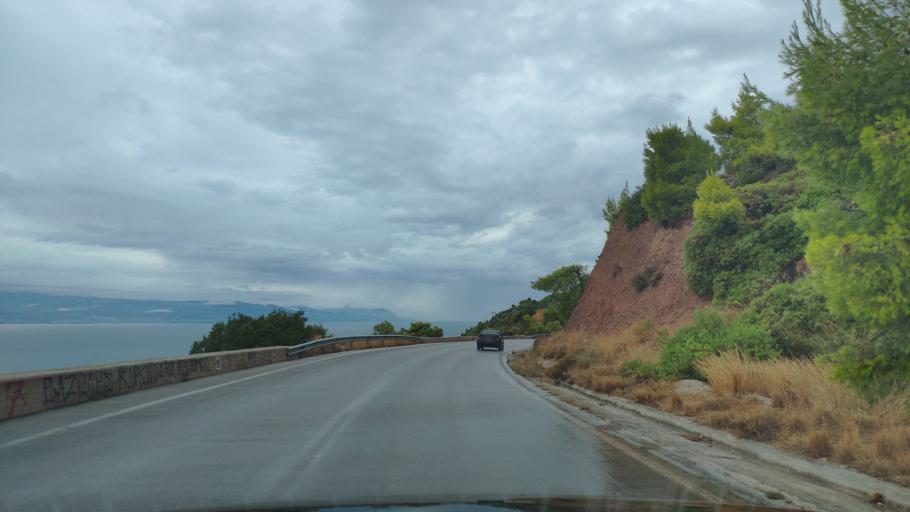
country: GR
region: Peloponnese
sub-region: Nomos Korinthias
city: Loutraki
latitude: 37.9839
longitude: 22.9698
